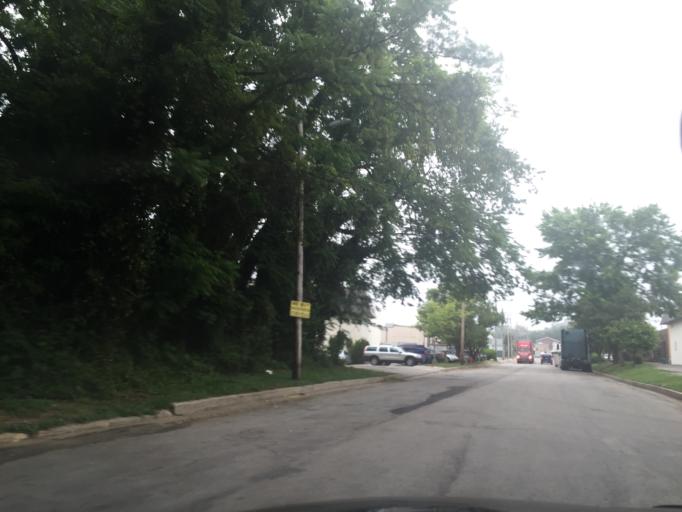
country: US
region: Maryland
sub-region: Baltimore County
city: Lochearn
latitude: 39.3516
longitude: -76.7011
